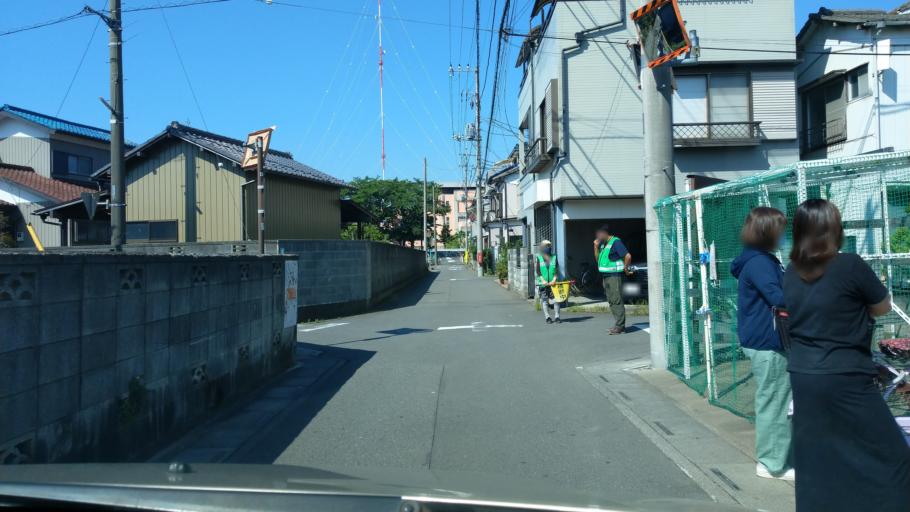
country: JP
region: Saitama
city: Yono
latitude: 35.8497
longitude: 139.6194
